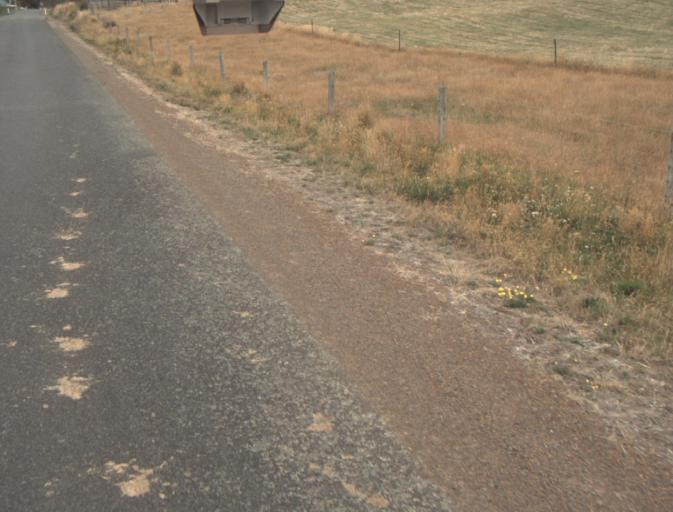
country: AU
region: Tasmania
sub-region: Dorset
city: Scottsdale
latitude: -41.4661
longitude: 147.5881
